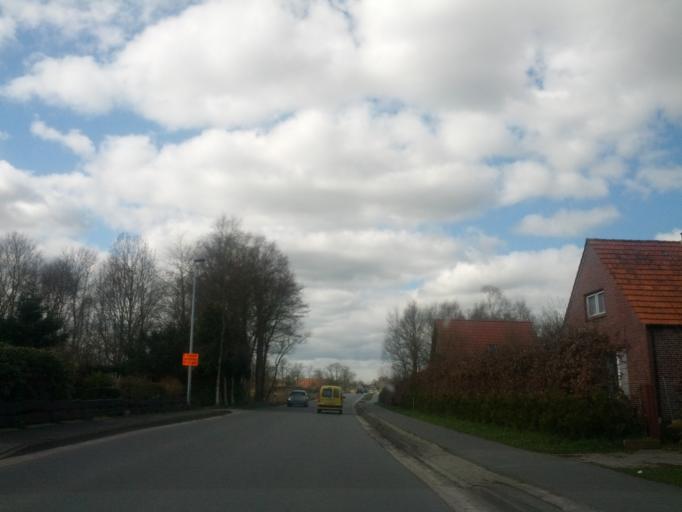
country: DE
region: Lower Saxony
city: Wittmund
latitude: 53.5958
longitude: 7.7417
